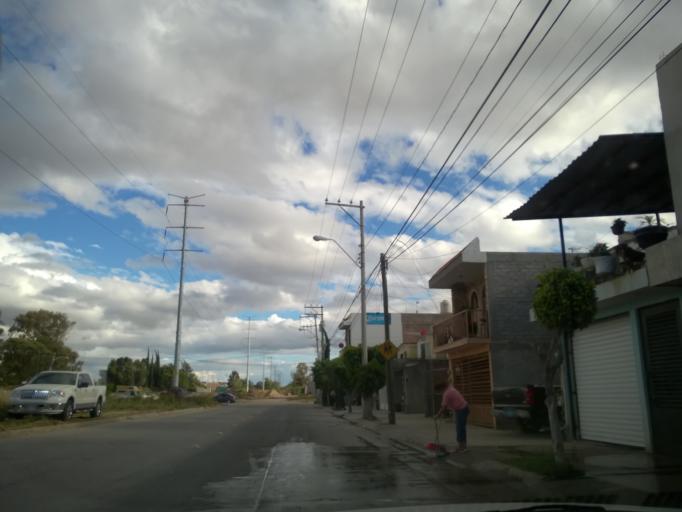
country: MX
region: Guanajuato
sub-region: Leon
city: Fraccionamiento Paraiso Real
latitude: 21.0717
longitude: -101.6115
